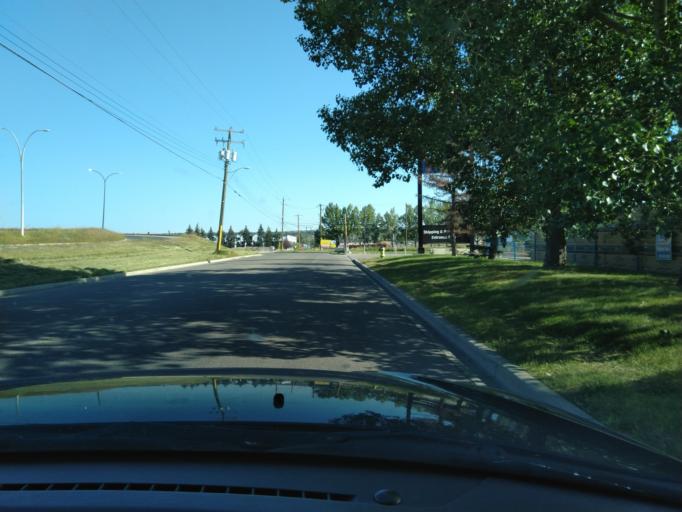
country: CA
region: Alberta
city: Calgary
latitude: 51.0805
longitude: -114.1874
